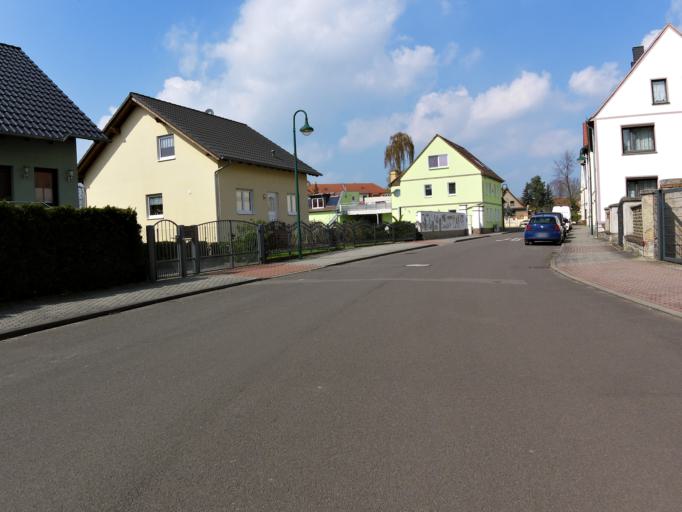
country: DE
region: Saxony
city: Markranstadt
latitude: 51.3225
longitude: 12.2567
